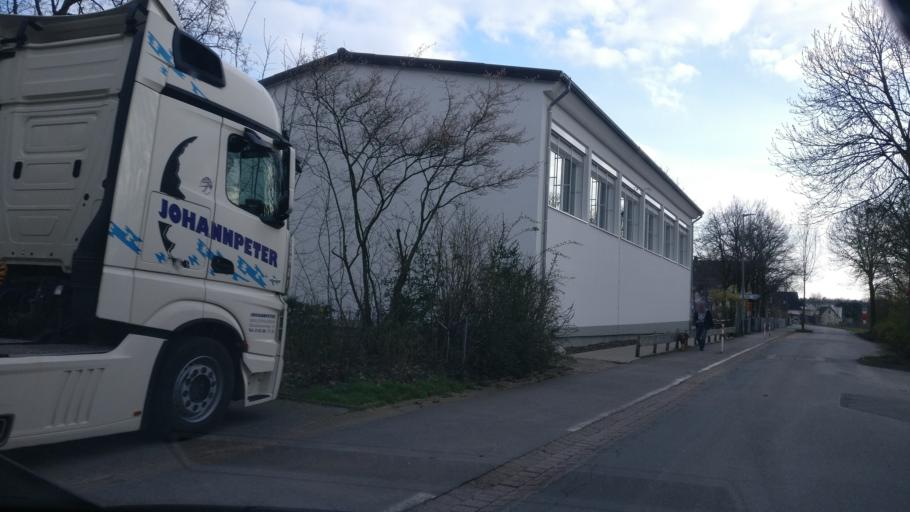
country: DE
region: North Rhine-Westphalia
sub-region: Regierungsbezirk Detmold
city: Lage
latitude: 52.0177
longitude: 8.7723
